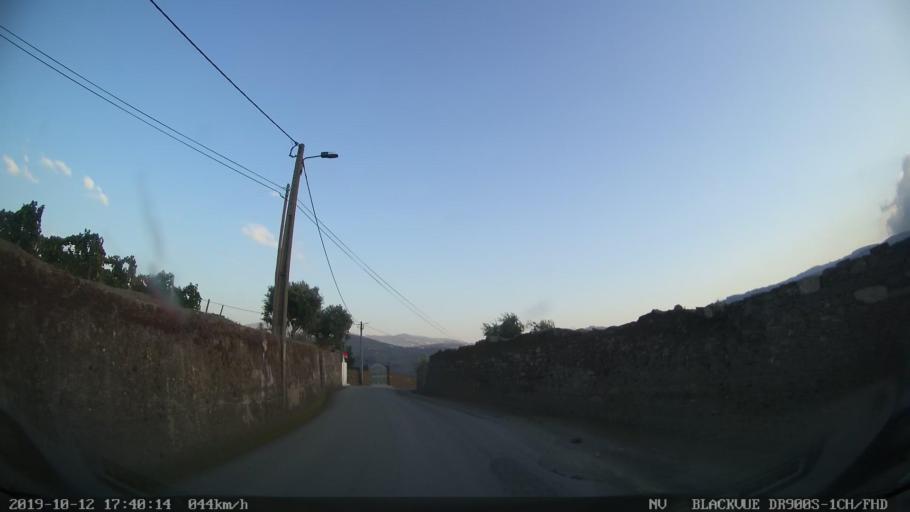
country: PT
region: Vila Real
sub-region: Peso da Regua
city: Godim
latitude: 41.1537
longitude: -7.8162
